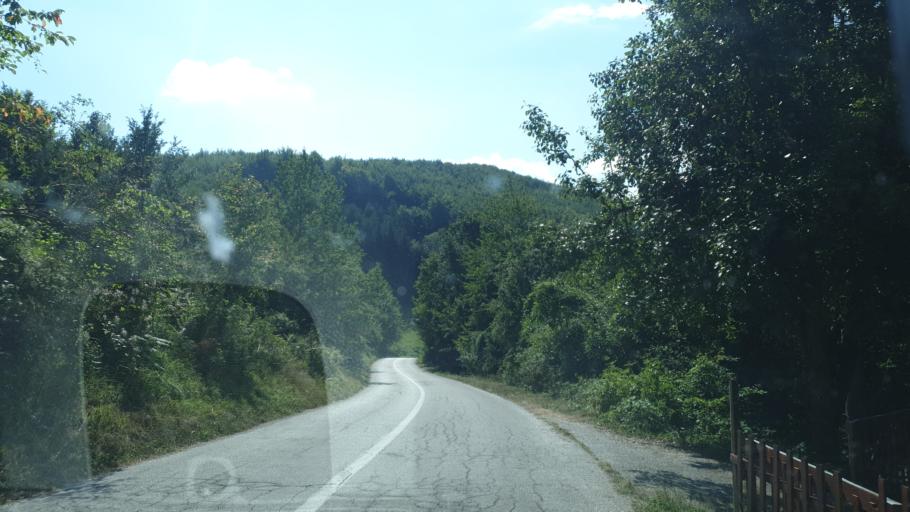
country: RS
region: Central Serbia
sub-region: Zlatiborski Okrug
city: Cajetina
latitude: 43.6809
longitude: 19.8504
